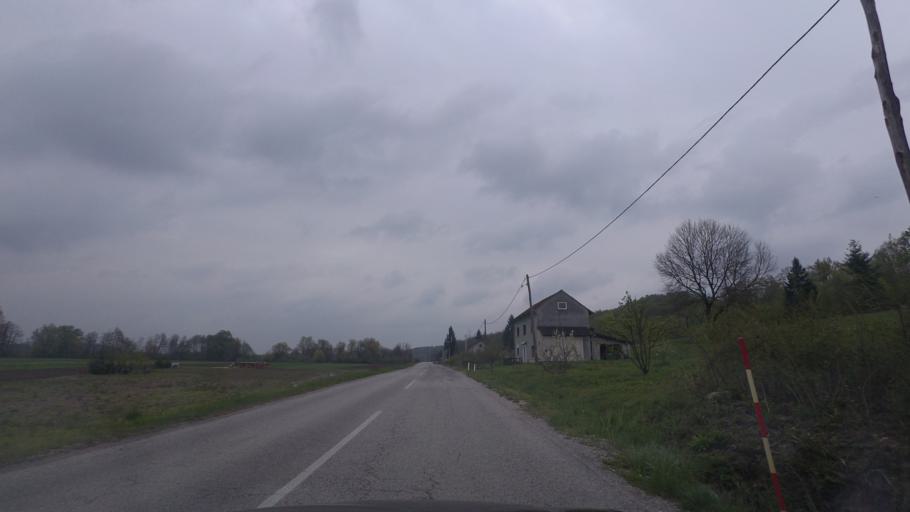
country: HR
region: Karlovacka
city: Ozalj
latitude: 45.6320
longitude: 15.5472
